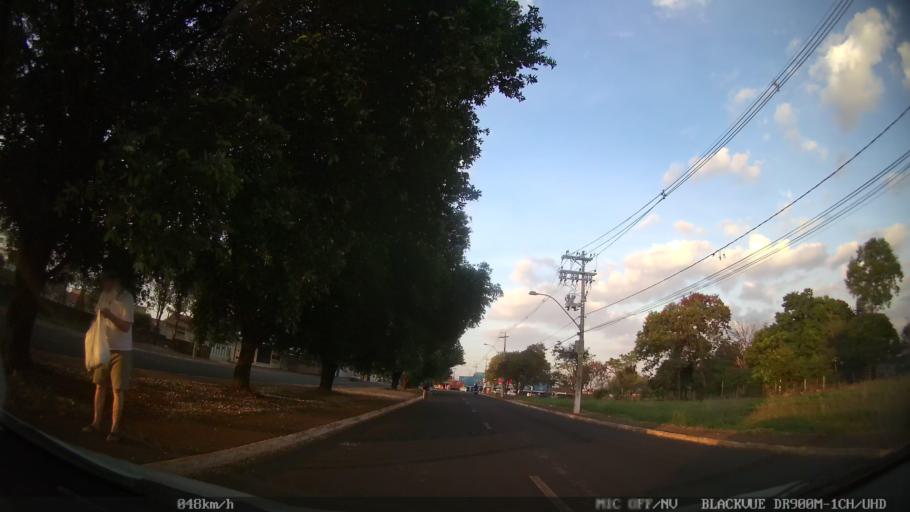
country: BR
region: Sao Paulo
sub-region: Ribeirao Preto
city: Ribeirao Preto
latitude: -21.1261
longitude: -47.8279
